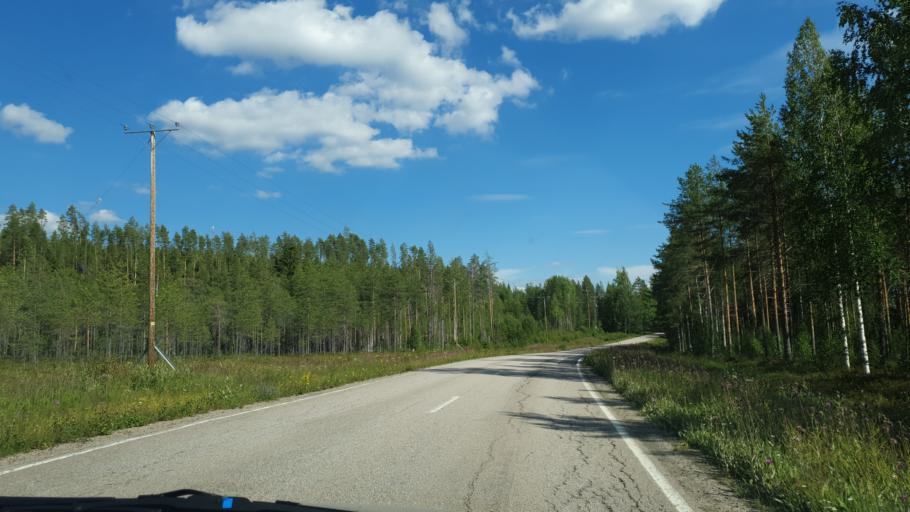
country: FI
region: Kainuu
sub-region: Kehys-Kainuu
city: Kuhmo
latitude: 64.1978
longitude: 29.1457
